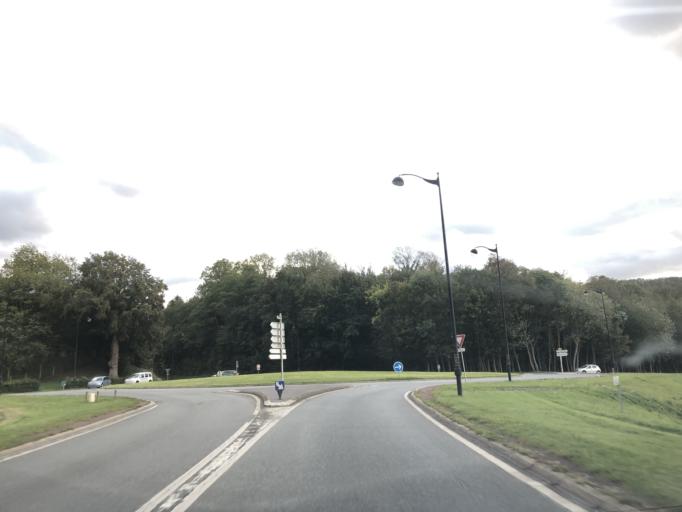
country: FR
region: Haute-Normandie
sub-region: Departement de la Seine-Maritime
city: Eu
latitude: 50.0536
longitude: 1.4037
